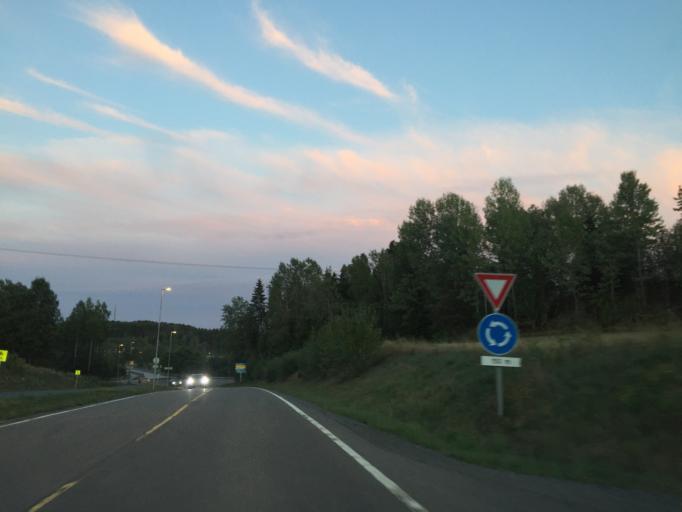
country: NO
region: Akershus
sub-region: Vestby
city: Vestby
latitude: 59.5178
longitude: 10.7191
